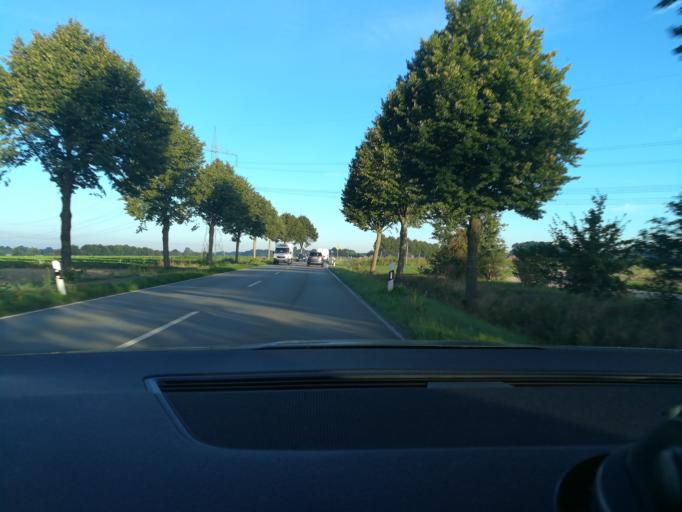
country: DE
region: North Rhine-Westphalia
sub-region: Regierungsbezirk Detmold
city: Minden
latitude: 52.3456
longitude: 8.8600
